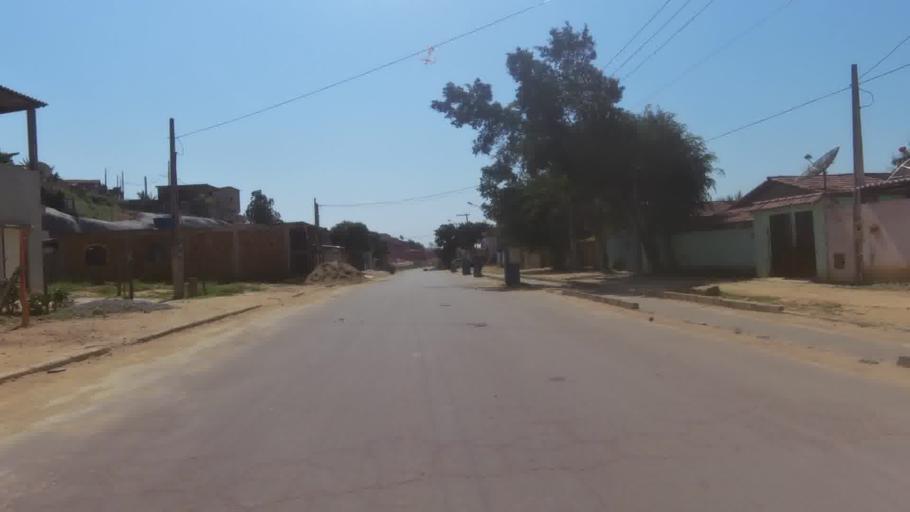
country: BR
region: Espirito Santo
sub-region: Itapemirim
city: Itapemirim
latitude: -21.0161
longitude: -40.8277
